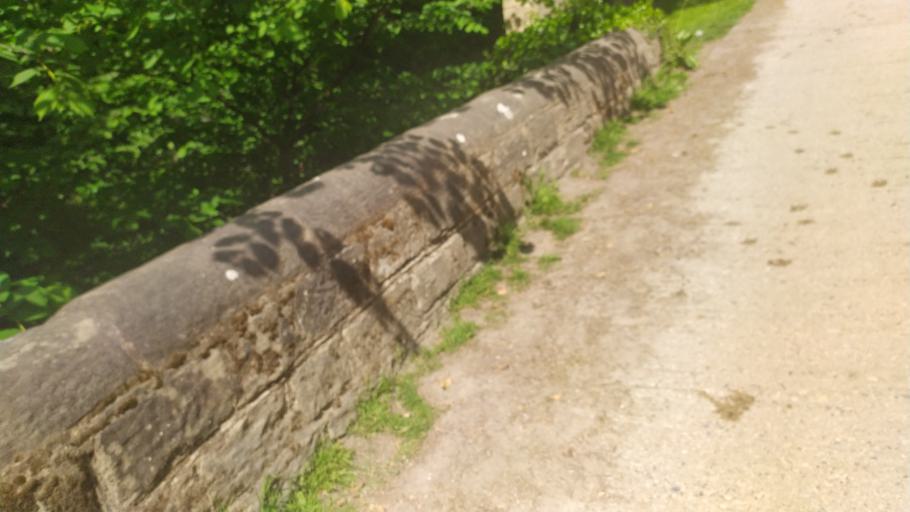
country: GB
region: England
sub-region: North Yorkshire
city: Pannal
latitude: 53.8964
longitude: -1.5356
